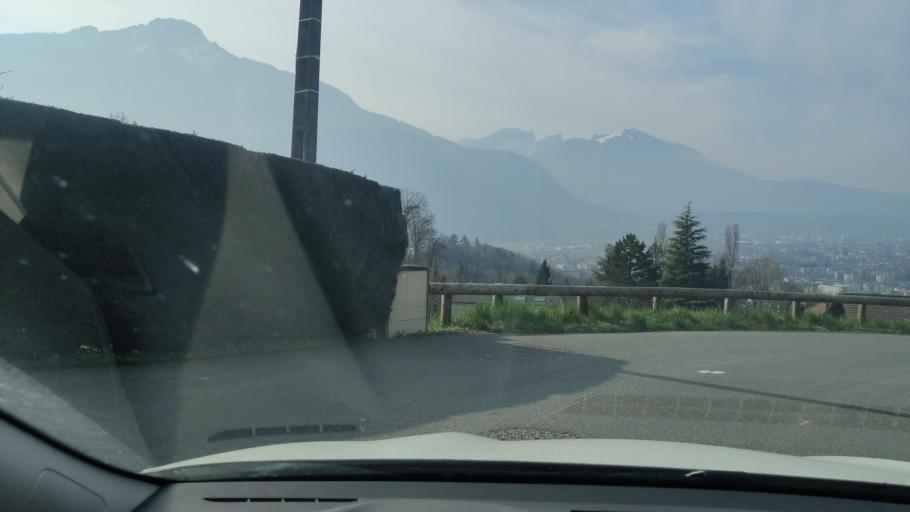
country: FR
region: Rhone-Alpes
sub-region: Departement de la Haute-Savoie
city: Ayse
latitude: 46.0881
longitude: 6.4197
